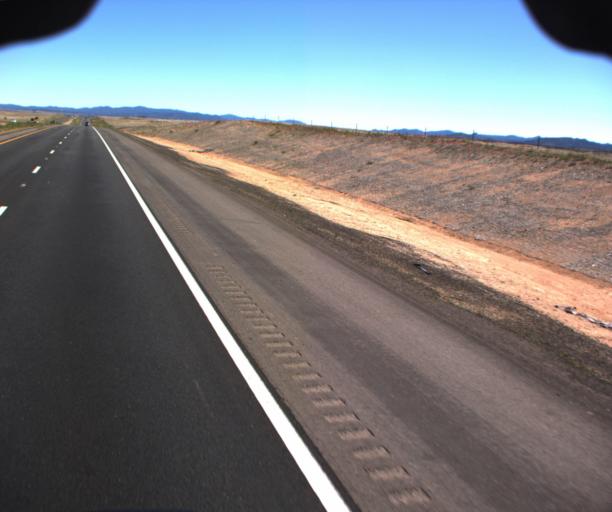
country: US
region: Arizona
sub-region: Yavapai County
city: Chino Valley
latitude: 34.6964
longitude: -112.4482
